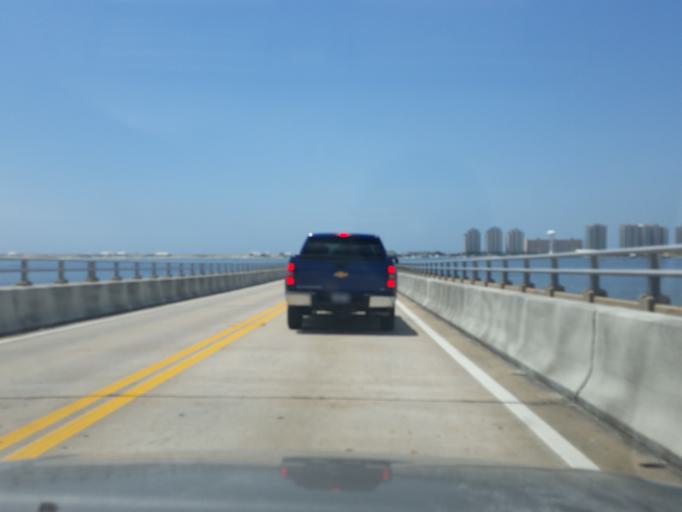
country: US
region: Florida
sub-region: Santa Rosa County
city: Navarre
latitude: 30.3939
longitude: -86.8631
